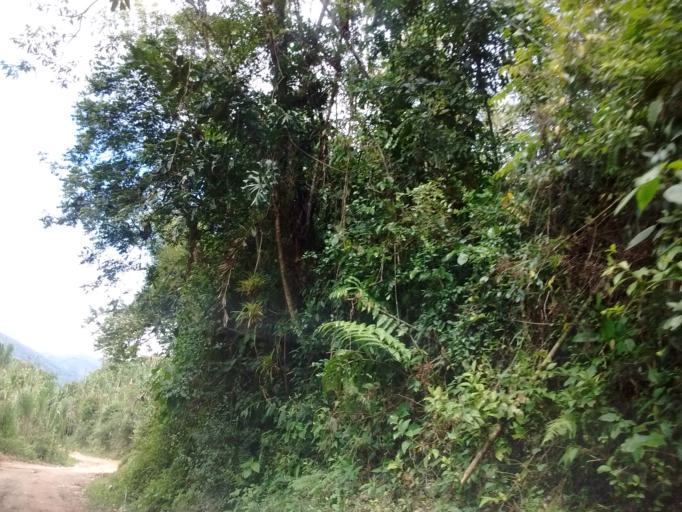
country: CO
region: Cauca
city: Morales
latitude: 2.6847
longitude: -76.7612
